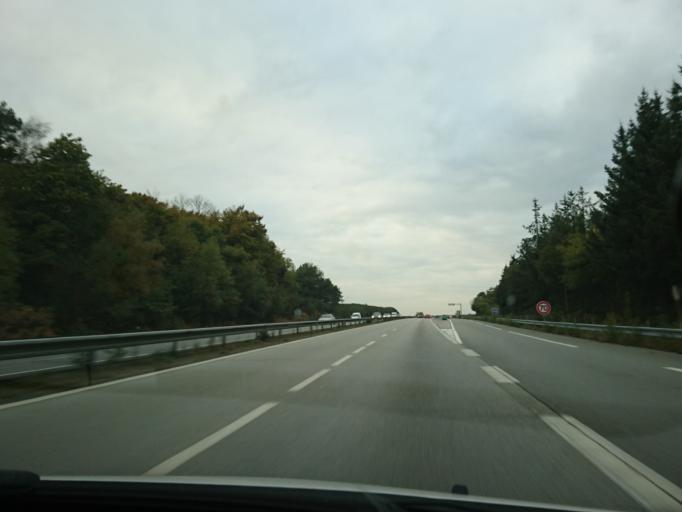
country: FR
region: Brittany
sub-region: Departement du Morbihan
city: Branderion
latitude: 47.7764
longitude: -3.1909
